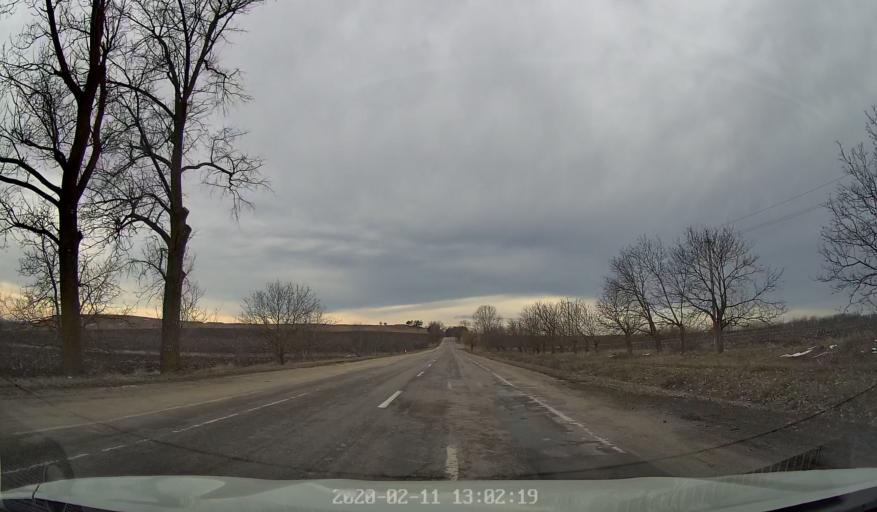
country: MD
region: Briceni
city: Briceni
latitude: 48.3164
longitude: 26.9835
